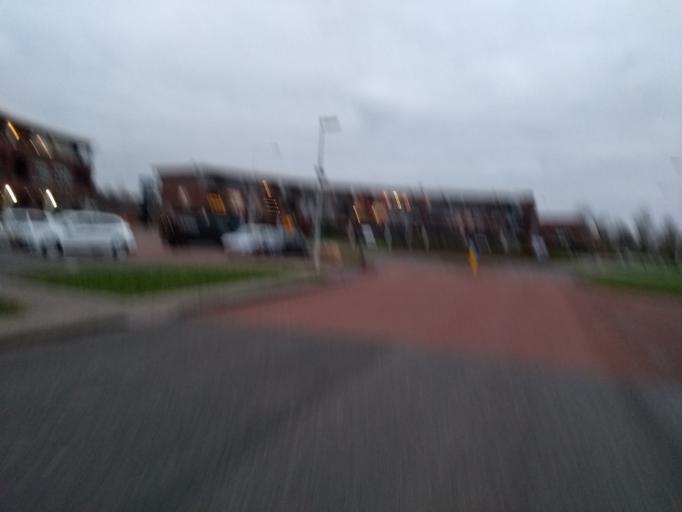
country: NL
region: Friesland
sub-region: Sudwest Fryslan
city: Sneek
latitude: 53.0179
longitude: 5.6626
